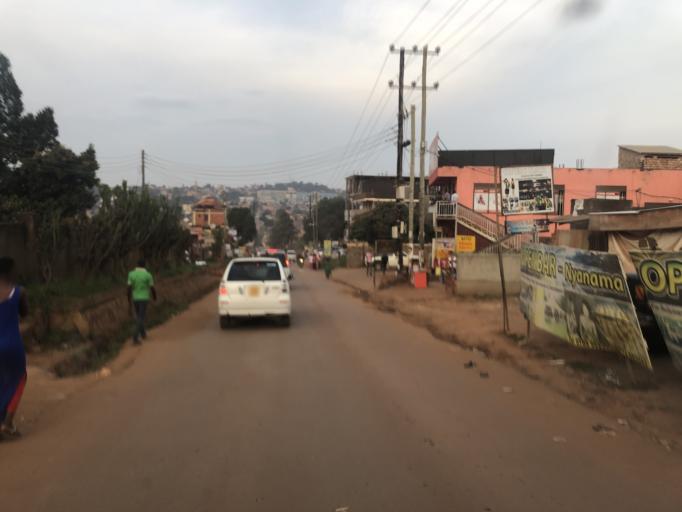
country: UG
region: Central Region
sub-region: Kampala District
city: Kampala
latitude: 0.2725
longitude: 32.5541
